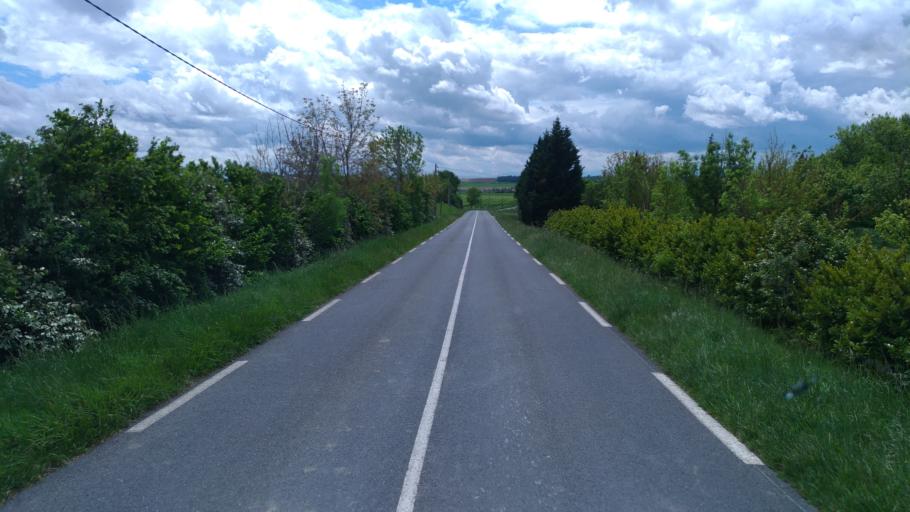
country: FR
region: Midi-Pyrenees
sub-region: Departement de la Haute-Garonne
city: Auriac-sur-Vendinelle
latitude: 43.4570
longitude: 1.8183
